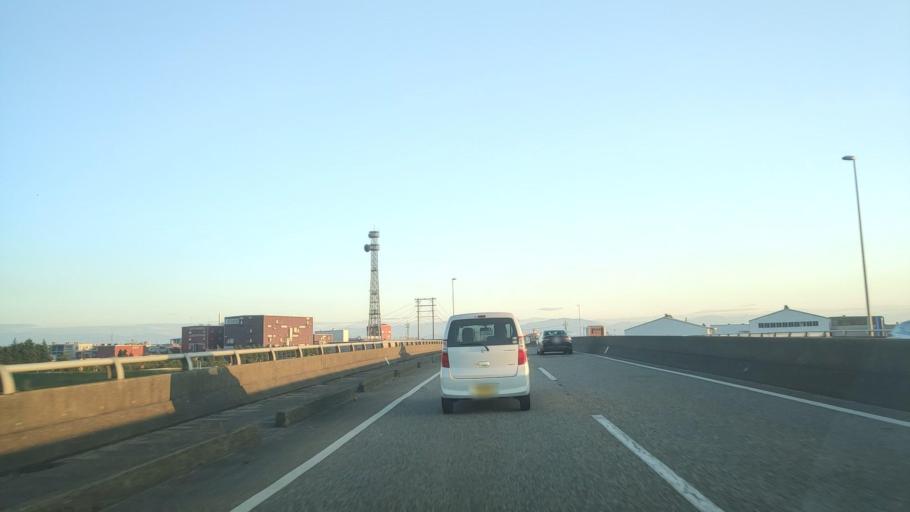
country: JP
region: Toyama
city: Takaoka
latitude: 36.7753
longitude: 137.0001
